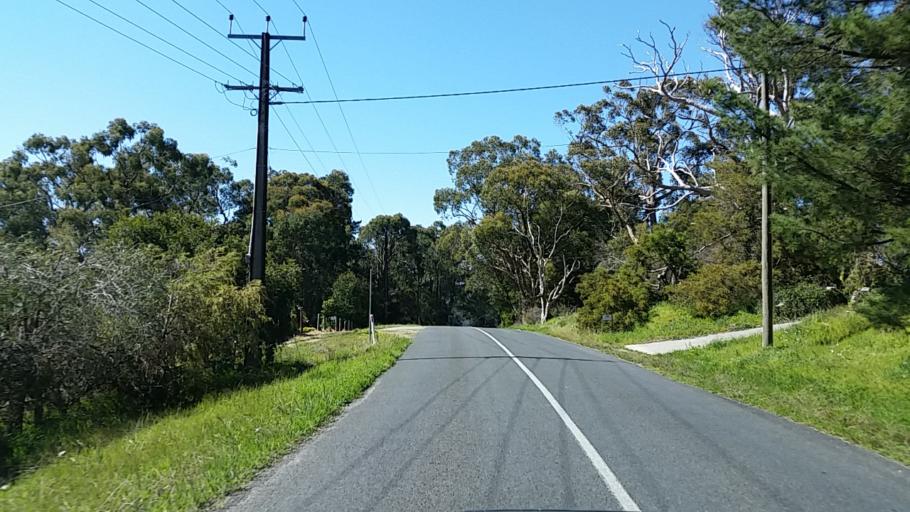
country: AU
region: South Australia
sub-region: Adelaide Hills
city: Bridgewater
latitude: -34.9527
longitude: 138.7591
